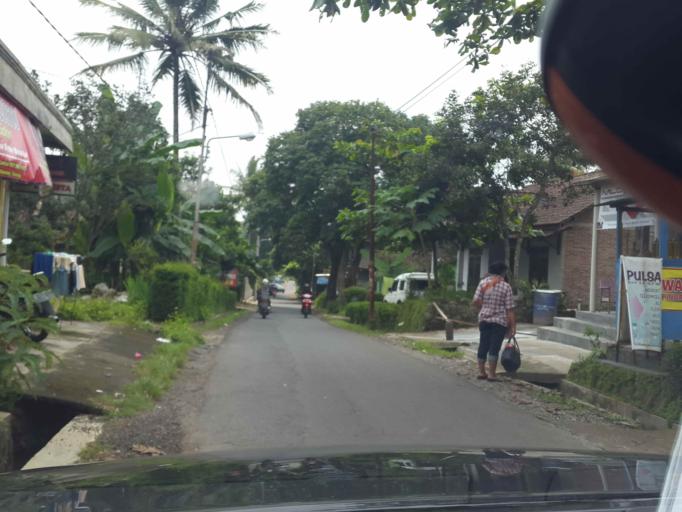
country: ID
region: Central Java
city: Salatiga
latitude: -7.3414
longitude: 110.5201
